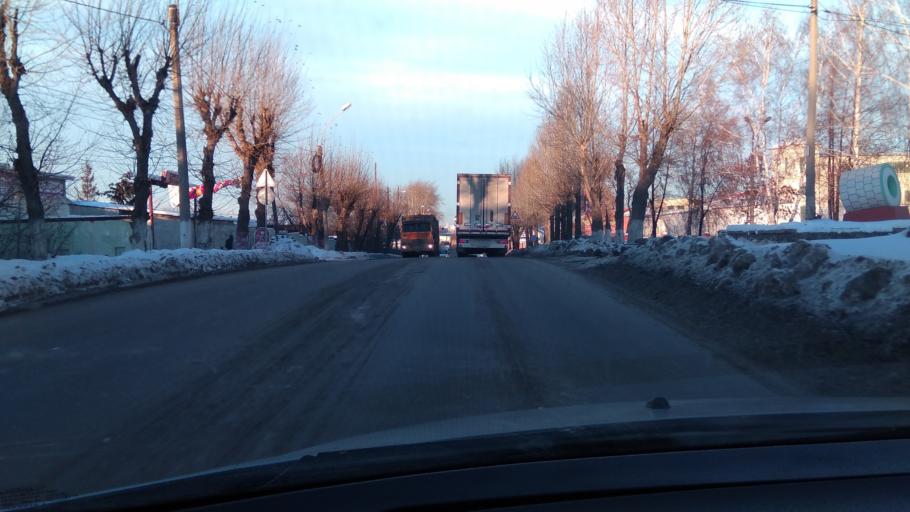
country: RU
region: Sverdlovsk
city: Sovkhoznyy
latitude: 56.7614
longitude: 60.6274
